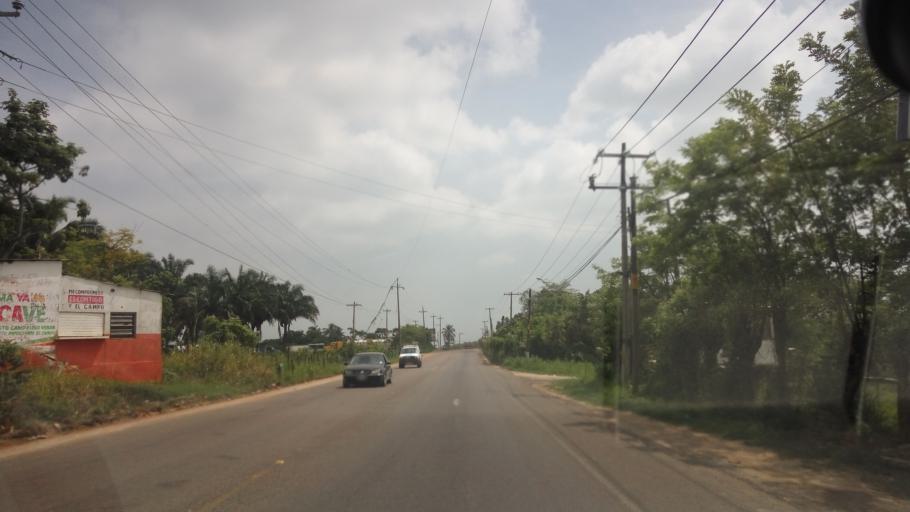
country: MX
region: Chiapas
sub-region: Reforma
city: El Carmen (El Limon)
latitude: 17.8797
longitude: -93.1500
